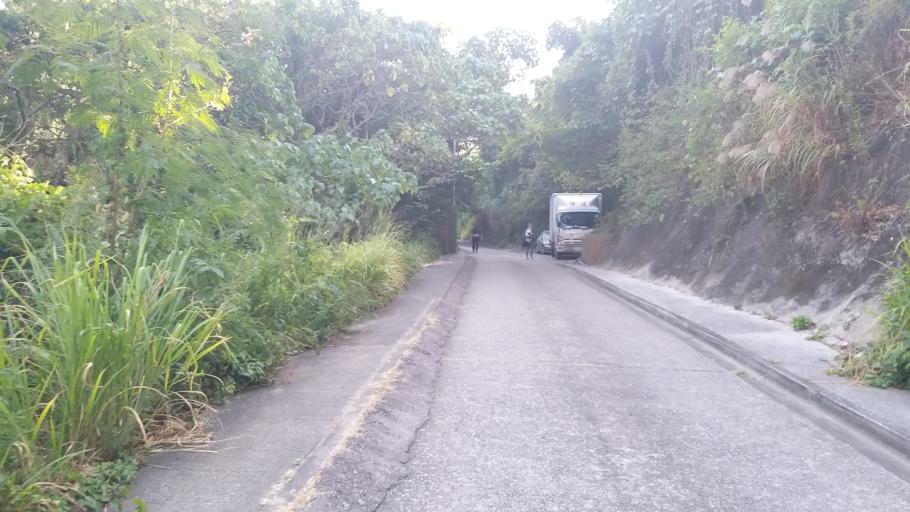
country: HK
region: Tuen Mun
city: Tuen Mun
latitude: 22.4066
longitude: 113.9856
